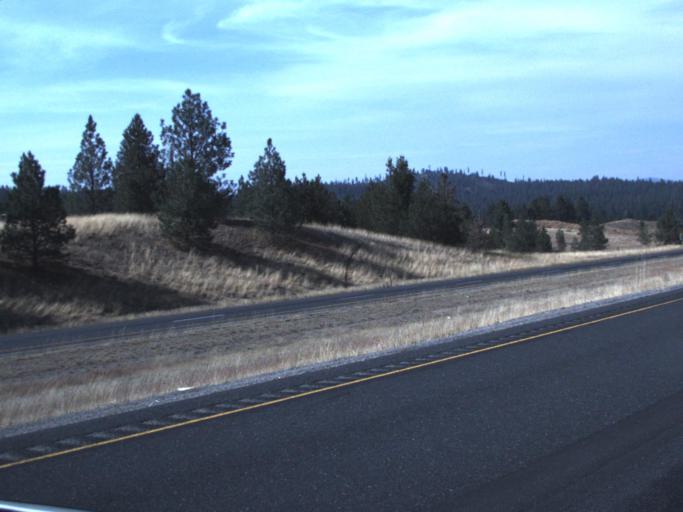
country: US
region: Washington
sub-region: Spokane County
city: Deer Park
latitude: 48.0528
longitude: -117.3438
